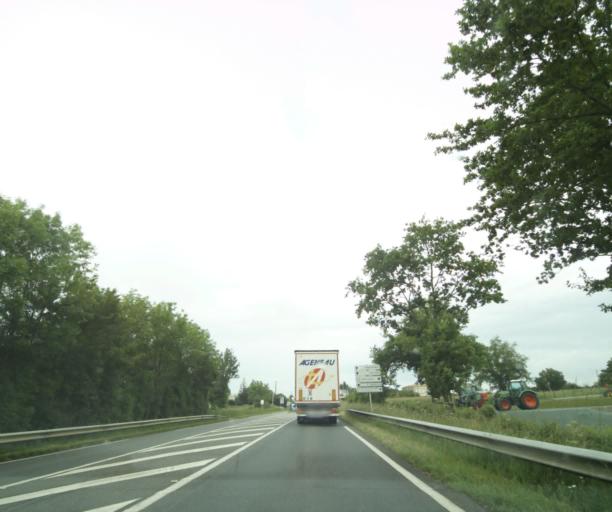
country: FR
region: Poitou-Charentes
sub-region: Departement des Deux-Sevres
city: Saint-Pardoux
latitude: 46.5677
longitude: -0.2993
